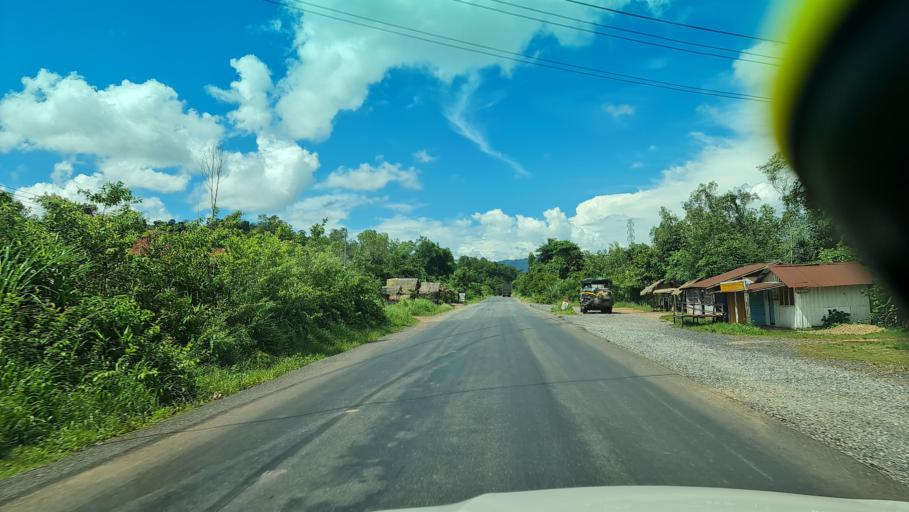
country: LA
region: Bolikhamxai
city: Pakkading
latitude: 18.2844
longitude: 104.0733
